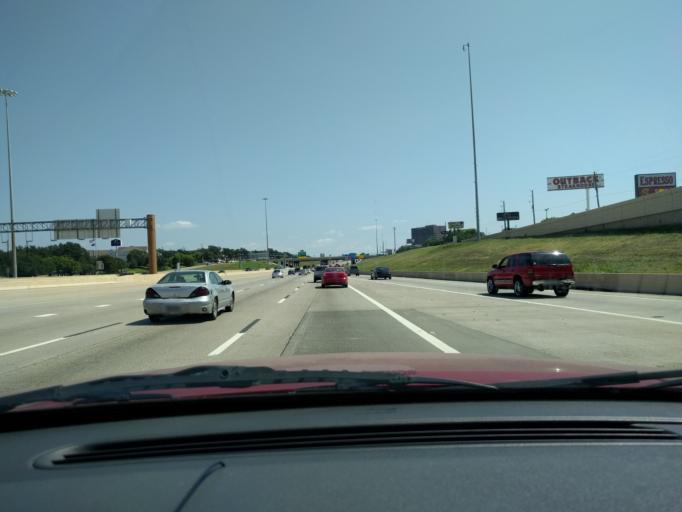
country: US
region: Texas
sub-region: Dallas County
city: Richardson
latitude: 32.9187
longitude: -96.7471
